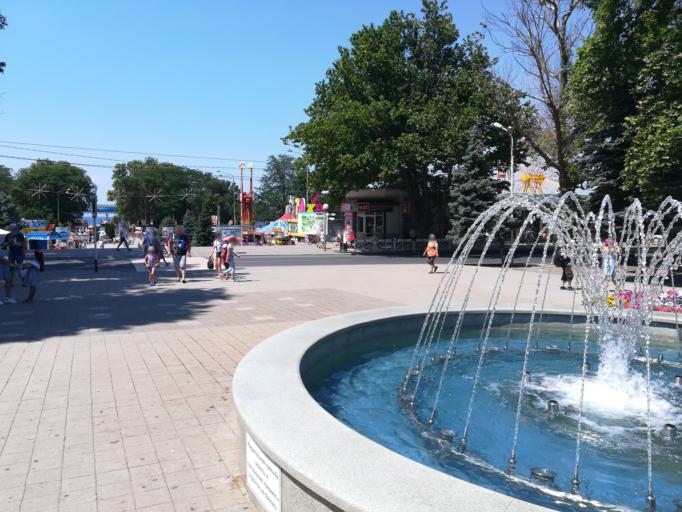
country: RU
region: Krasnodarskiy
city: Anapa
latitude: 44.8956
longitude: 37.3158
